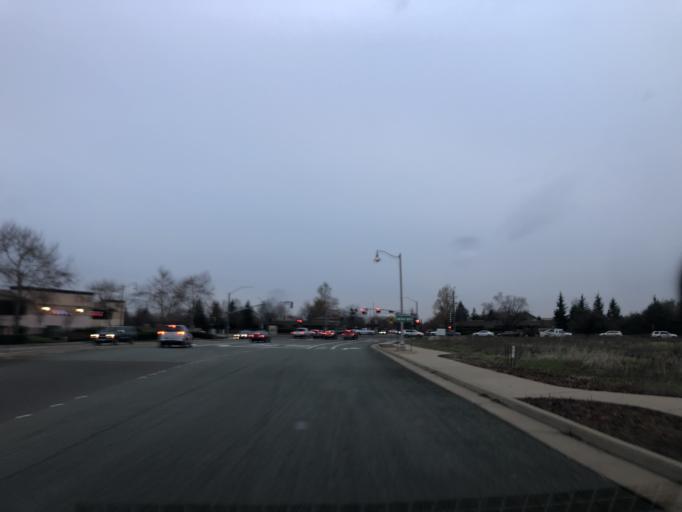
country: US
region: California
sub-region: Placer County
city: Lincoln
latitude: 38.8797
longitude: -121.2936
